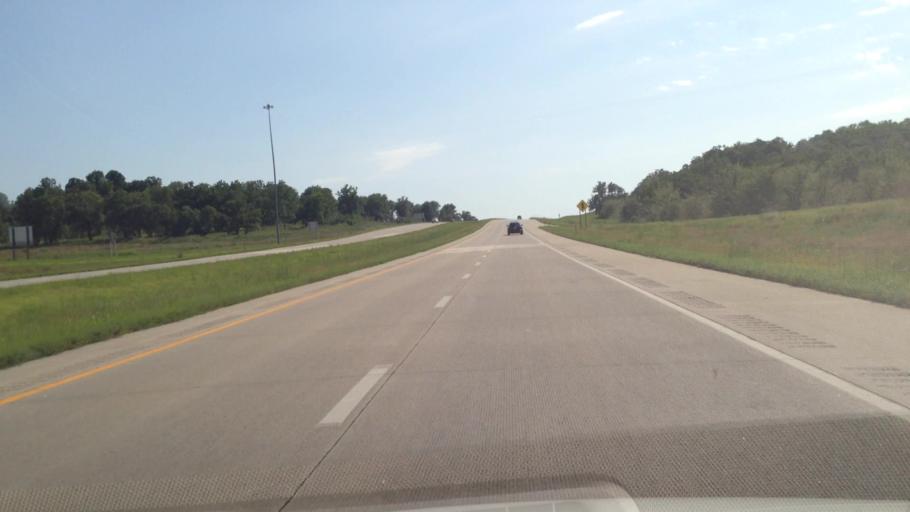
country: US
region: Kansas
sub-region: Linn County
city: Pleasanton
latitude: 38.2623
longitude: -94.6728
